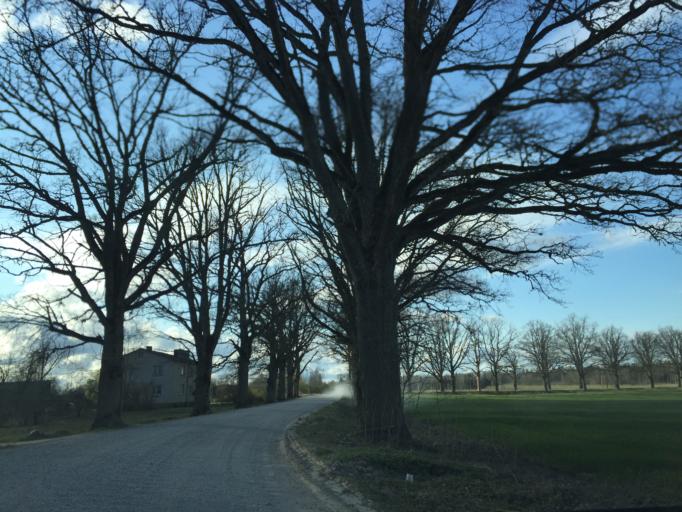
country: LV
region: Burtnieki
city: Matisi
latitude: 57.6147
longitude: 25.0784
